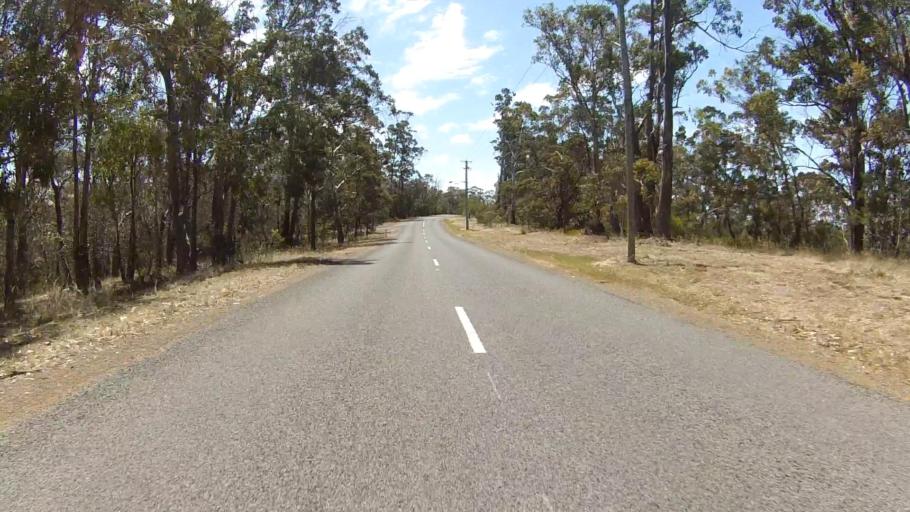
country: AU
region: Tasmania
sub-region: Clarence
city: Sandford
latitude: -43.0149
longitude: 147.4812
